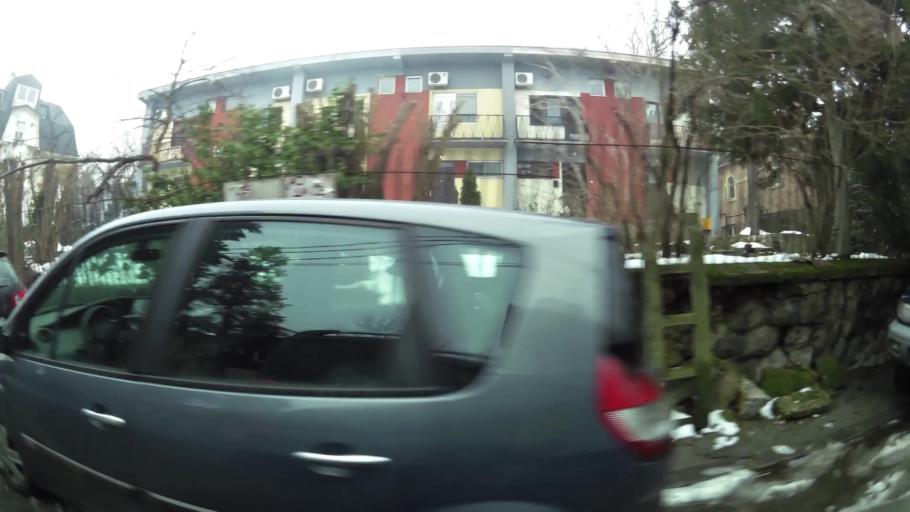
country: RS
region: Central Serbia
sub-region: Belgrade
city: Savski Venac
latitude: 44.7812
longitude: 20.4627
